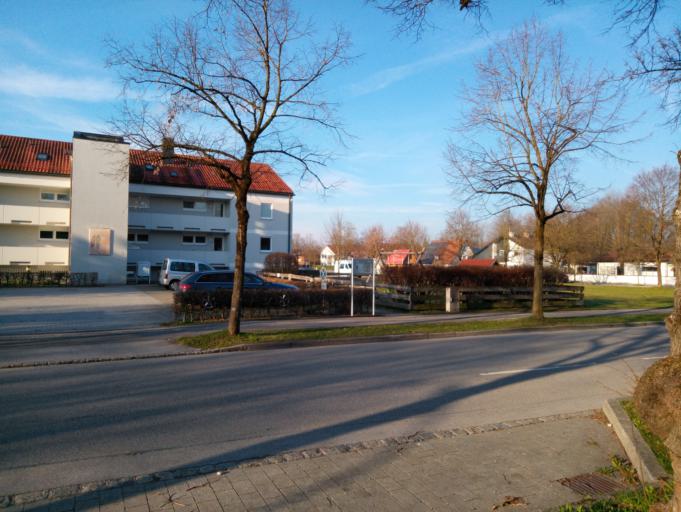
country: DE
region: Bavaria
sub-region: Upper Bavaria
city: Weilheim
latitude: 47.8426
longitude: 11.1529
